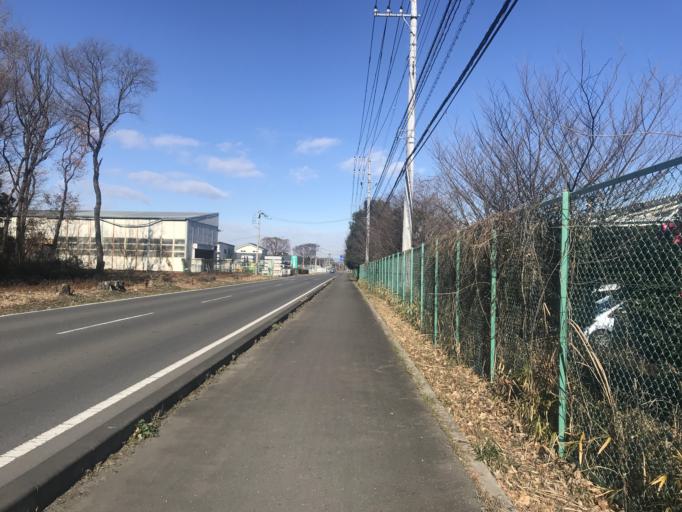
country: JP
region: Ibaraki
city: Yuki
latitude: 36.3478
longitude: 139.8783
